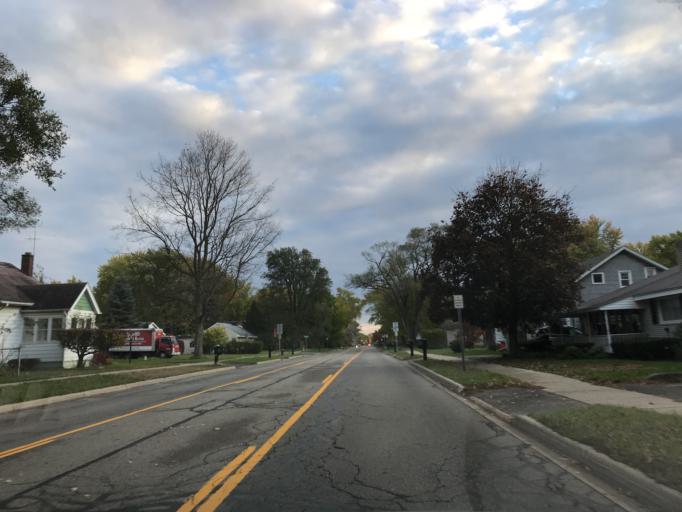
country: US
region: Michigan
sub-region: Oakland County
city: Farmington
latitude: 42.4465
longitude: -83.3171
